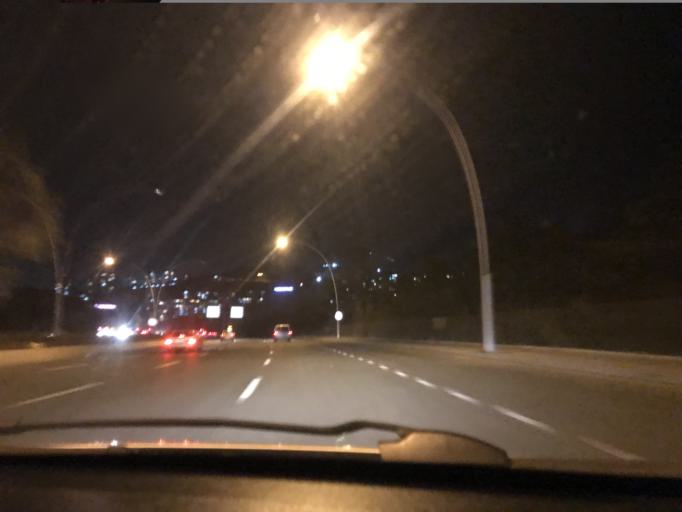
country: TR
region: Ankara
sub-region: Goelbasi
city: Golbasi
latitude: 39.8451
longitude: 32.8093
